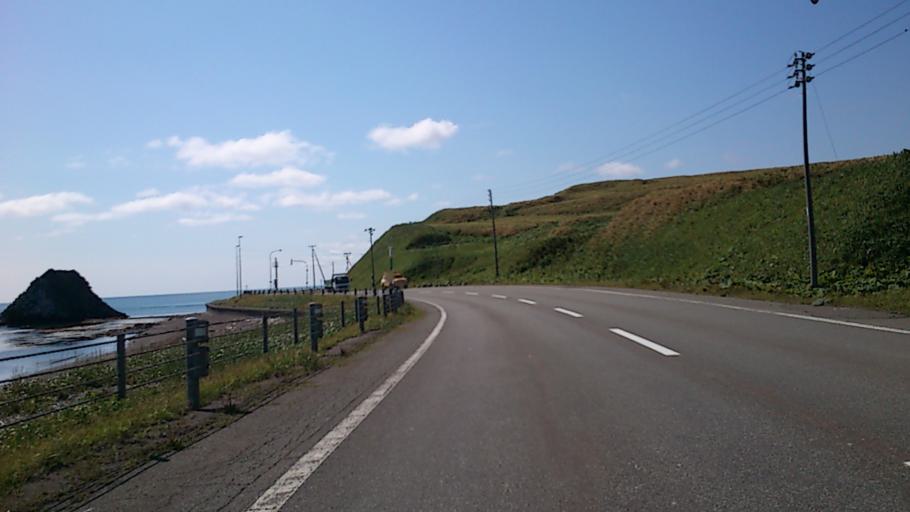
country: JP
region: Hokkaido
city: Makubetsu
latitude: 45.4992
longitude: 141.9647
